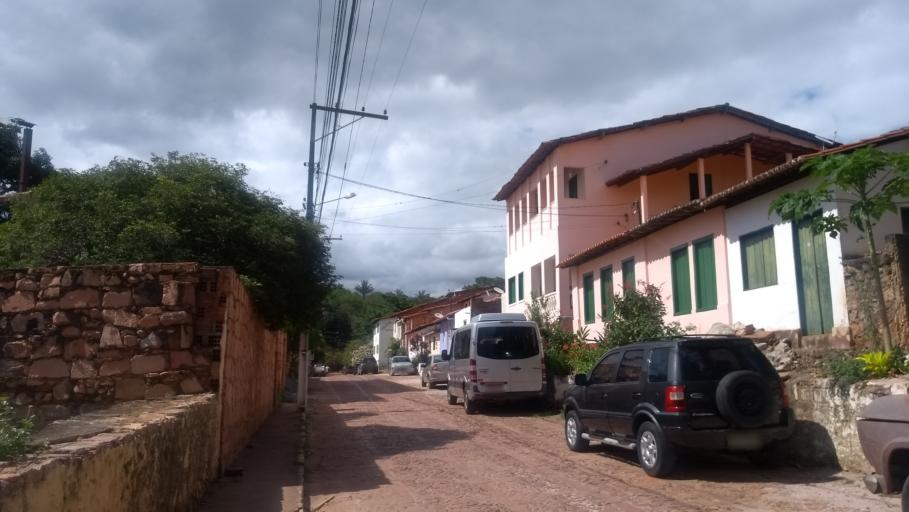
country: BR
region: Bahia
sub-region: Andarai
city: Vera Cruz
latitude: -12.5656
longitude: -41.3897
